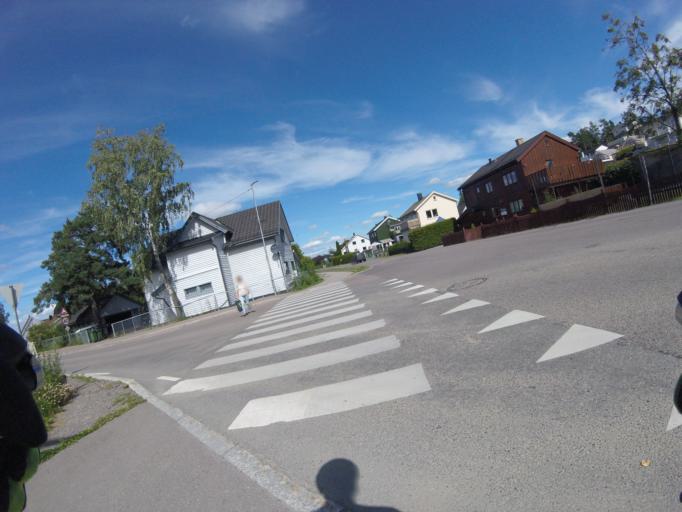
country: NO
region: Akershus
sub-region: Skedsmo
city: Lillestrom
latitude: 59.9418
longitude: 11.0150
